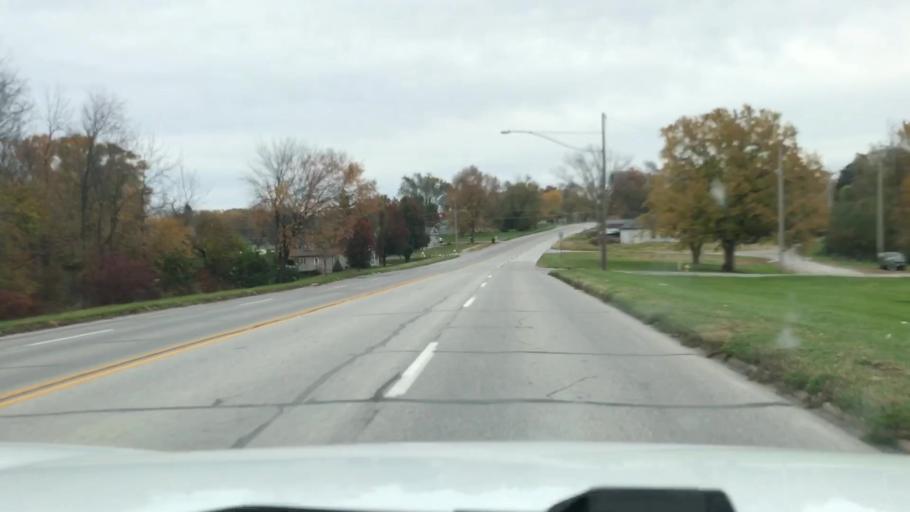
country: US
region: Iowa
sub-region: Lee County
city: Keokuk
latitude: 40.3896
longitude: -91.4128
